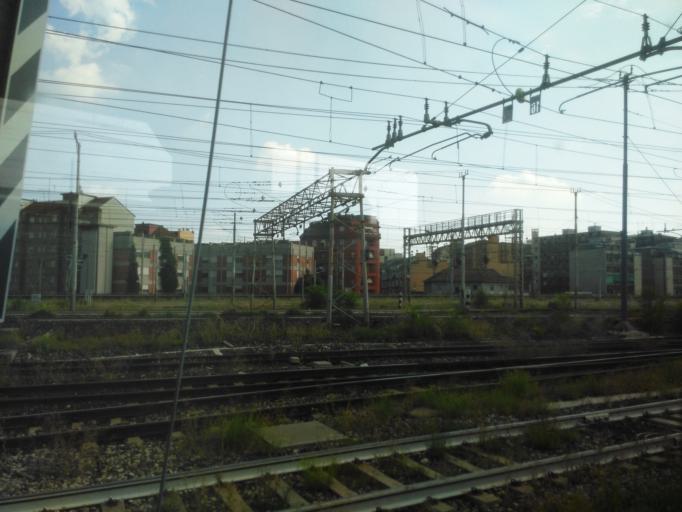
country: IT
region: Lombardy
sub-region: Citta metropolitana di Milano
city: Milano
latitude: 45.4960
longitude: 9.2143
